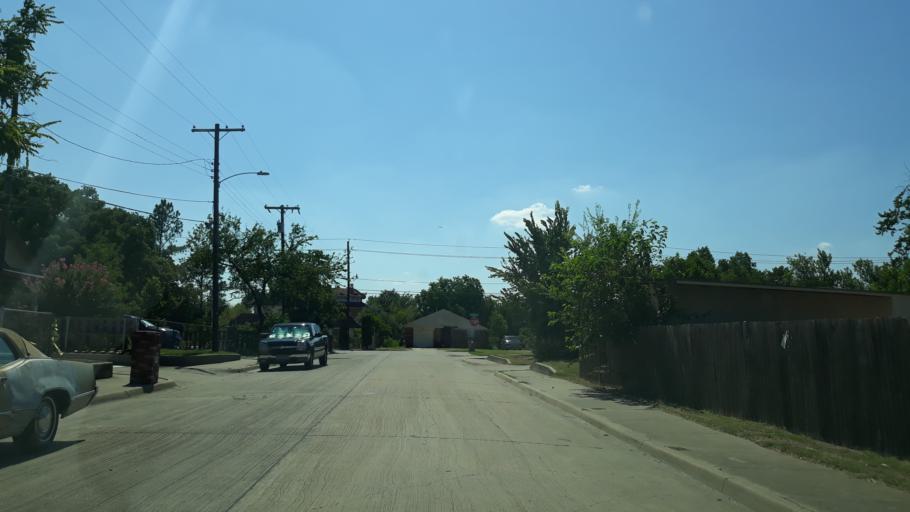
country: US
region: Texas
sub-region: Dallas County
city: Irving
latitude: 32.8210
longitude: -97.0017
